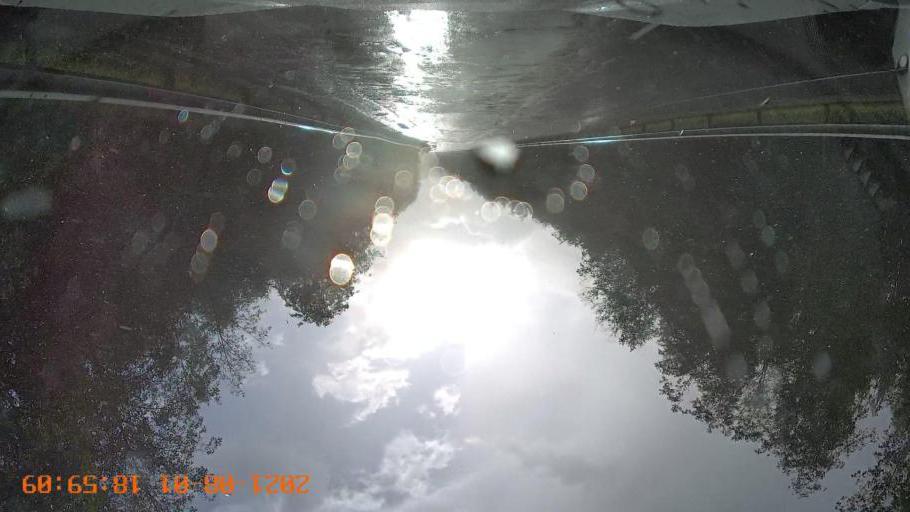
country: RU
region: Leningrad
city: Podporozh'ye
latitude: 60.9003
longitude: 34.6710
